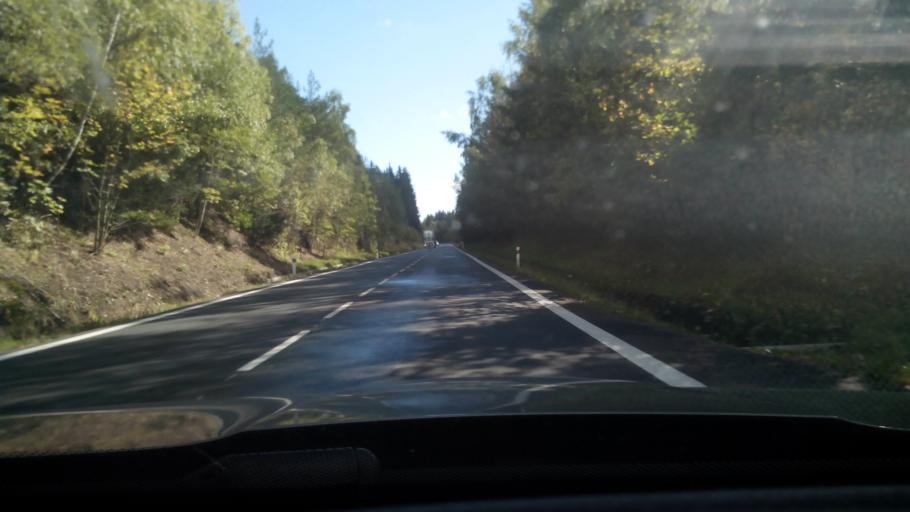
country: CZ
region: Jihocesky
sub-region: Okres Prachatice
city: Zdikov
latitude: 49.0712
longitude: 13.7142
